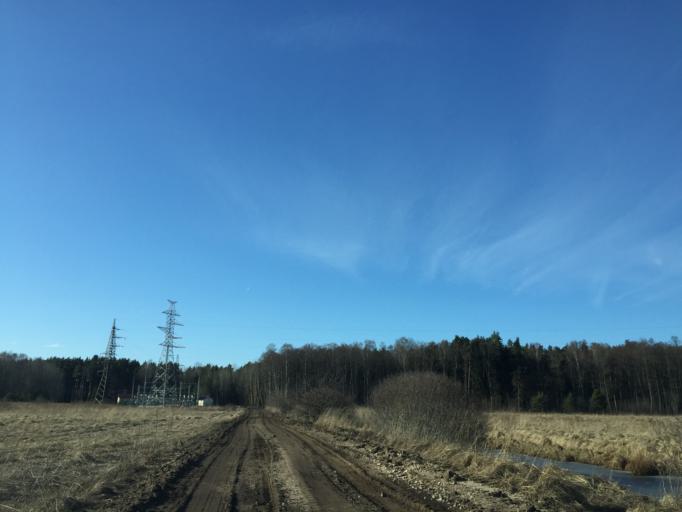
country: LV
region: Babite
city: Pinki
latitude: 56.9652
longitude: 23.8880
